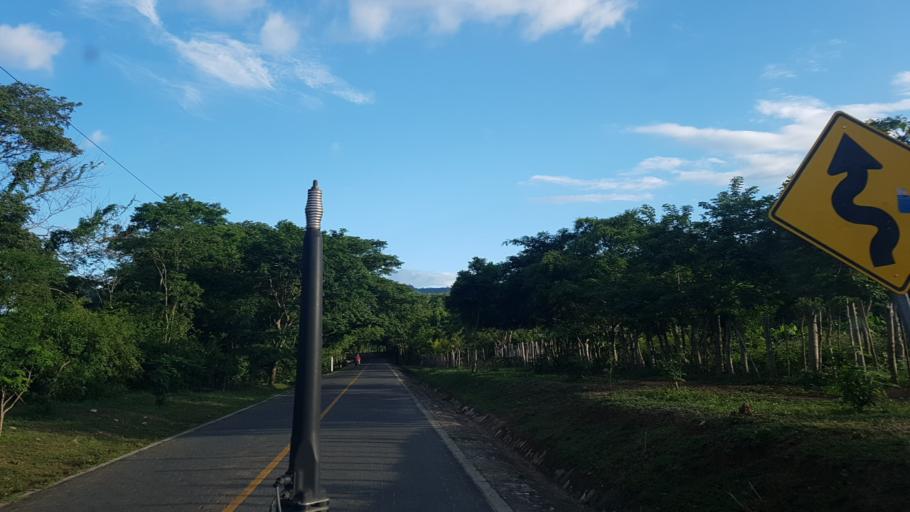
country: NI
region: Nueva Segovia
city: Ocotal
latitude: 13.6430
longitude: -86.5931
